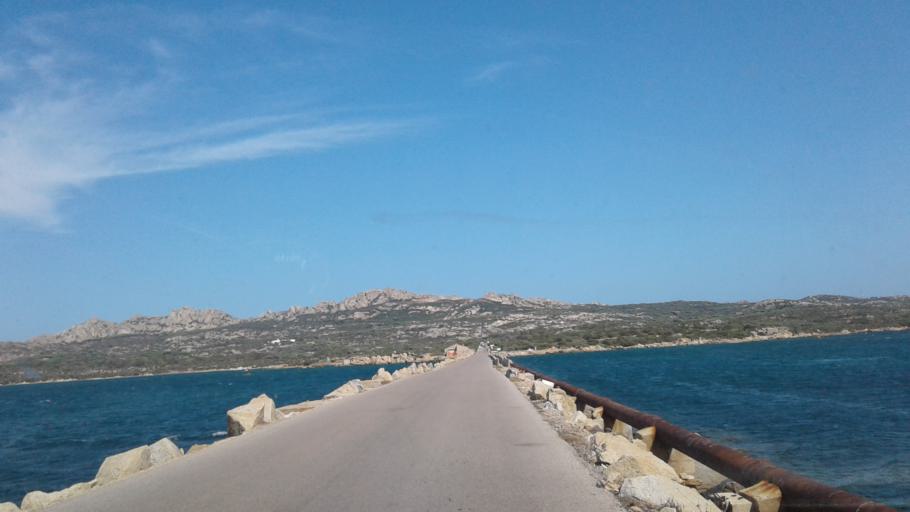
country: IT
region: Sardinia
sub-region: Provincia di Olbia-Tempio
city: La Maddalena
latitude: 41.2161
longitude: 9.4423
